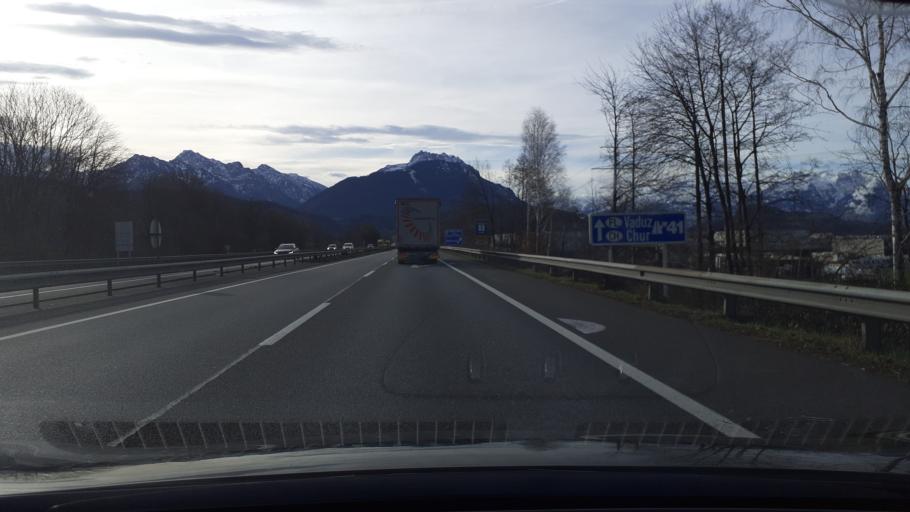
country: AT
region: Vorarlberg
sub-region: Politischer Bezirk Feldkirch
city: Rankweil
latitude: 47.2845
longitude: 9.6250
